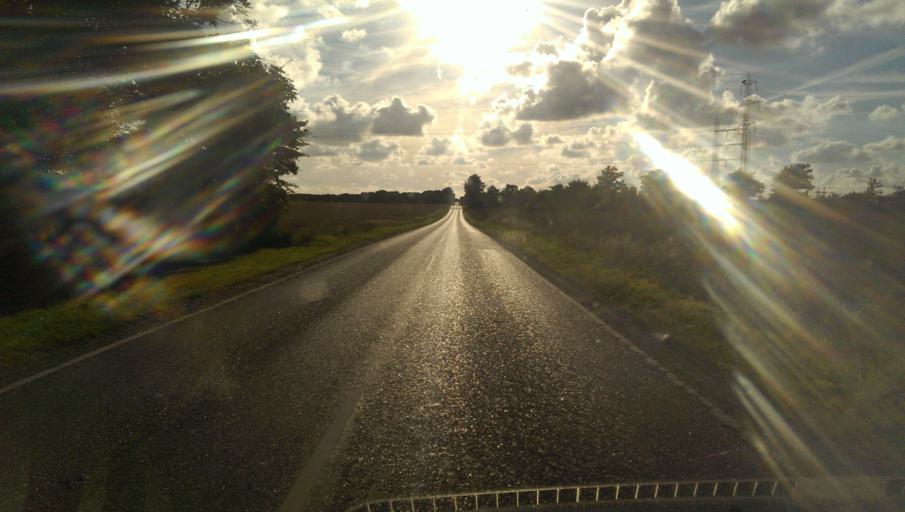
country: DK
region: South Denmark
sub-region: Esbjerg Kommune
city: Esbjerg
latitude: 55.5180
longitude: 8.5029
